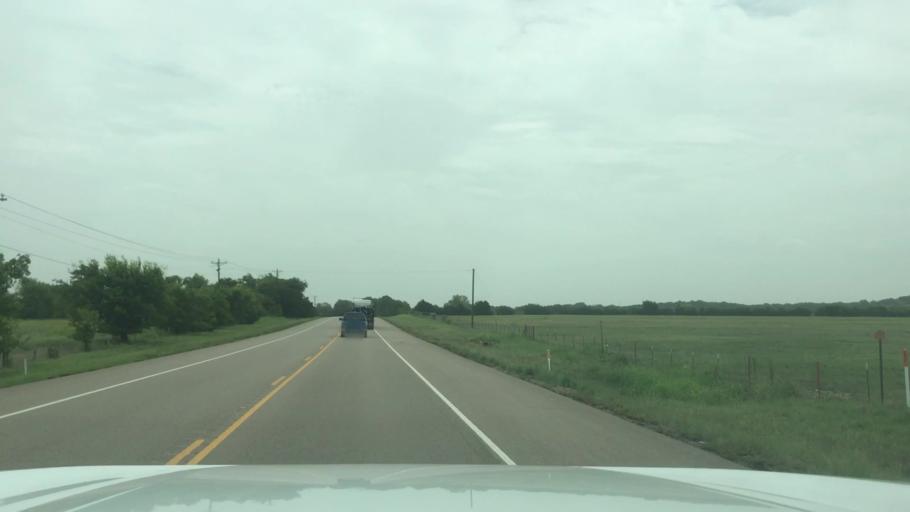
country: US
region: Texas
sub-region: Bosque County
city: Meridian
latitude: 31.9394
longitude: -97.7089
